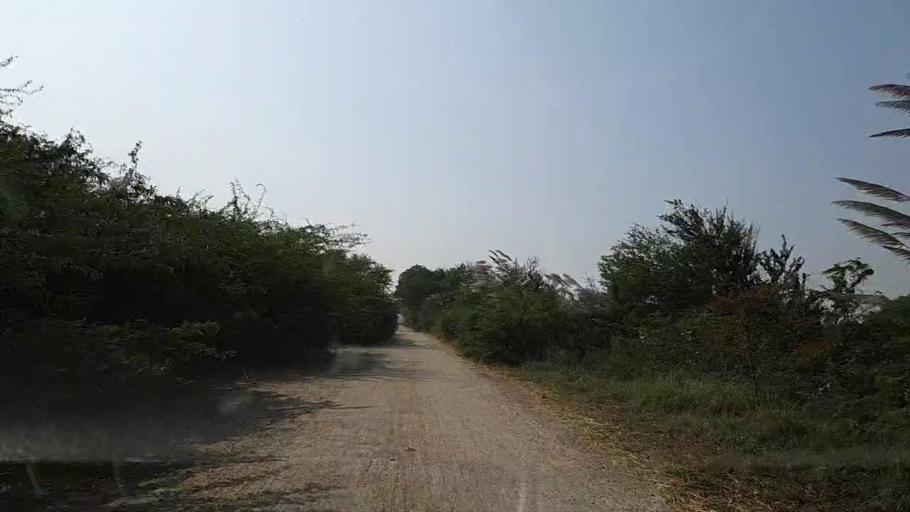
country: PK
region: Sindh
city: Mirpur Sakro
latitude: 24.5297
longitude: 67.5573
